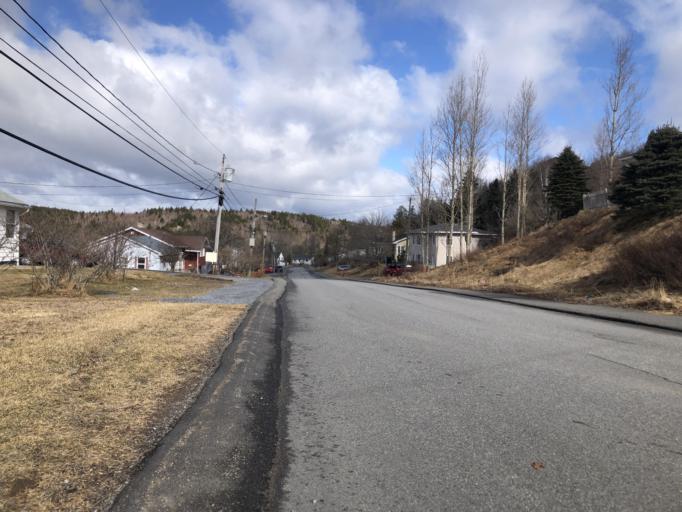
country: CA
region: New Brunswick
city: Saint John
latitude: 45.3196
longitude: -66.0094
